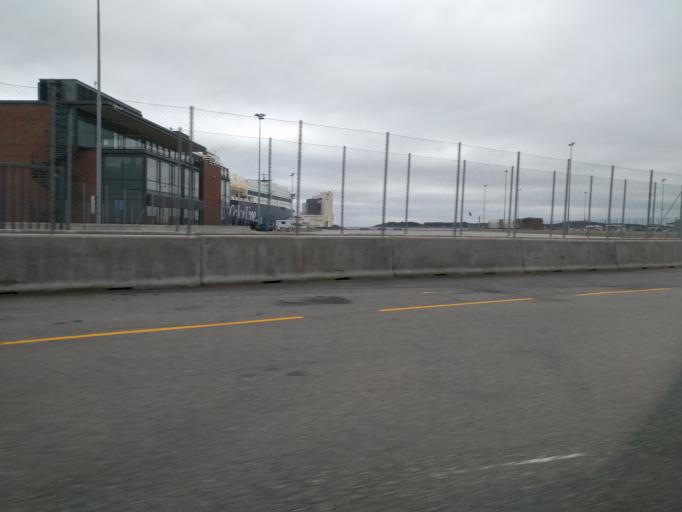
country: NO
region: Vest-Agder
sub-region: Kristiansand
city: Kristiansand
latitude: 58.1448
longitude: 7.9830
